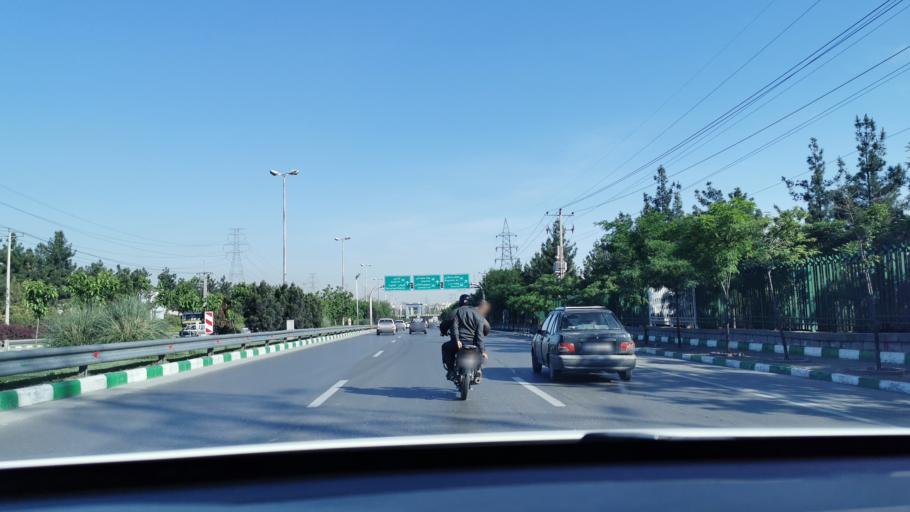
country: IR
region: Razavi Khorasan
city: Mashhad
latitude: 36.2591
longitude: 59.5876
